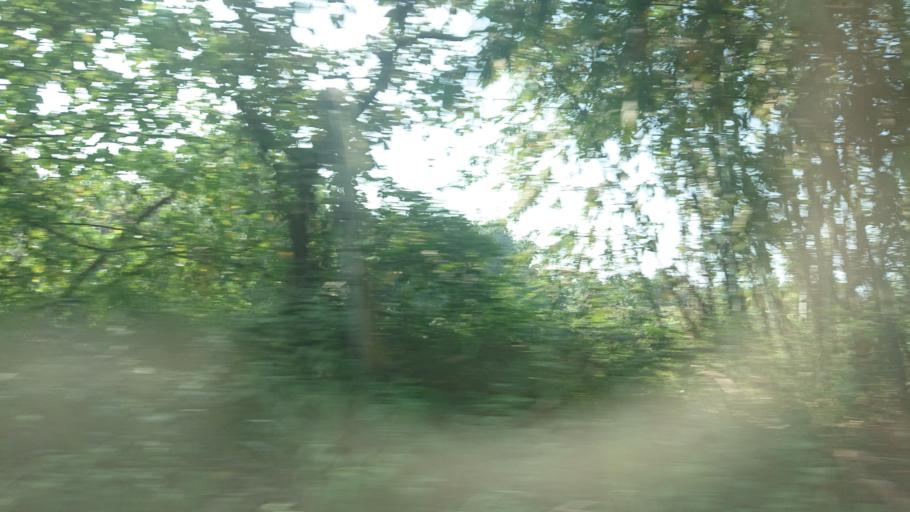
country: TW
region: Taiwan
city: Lugu
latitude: 23.7204
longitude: 120.6704
